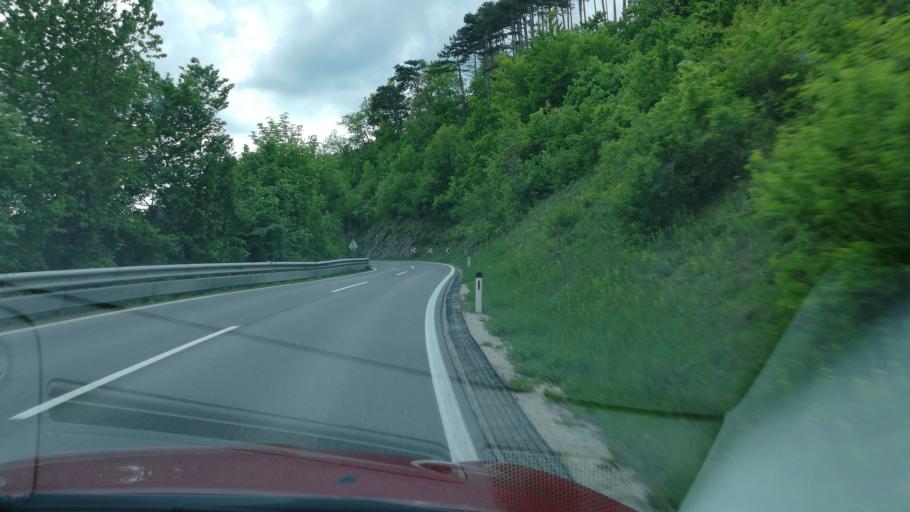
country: AT
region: Lower Austria
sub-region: Politischer Bezirk Baden
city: Heiligenkreuz
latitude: 48.0250
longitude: 16.1588
